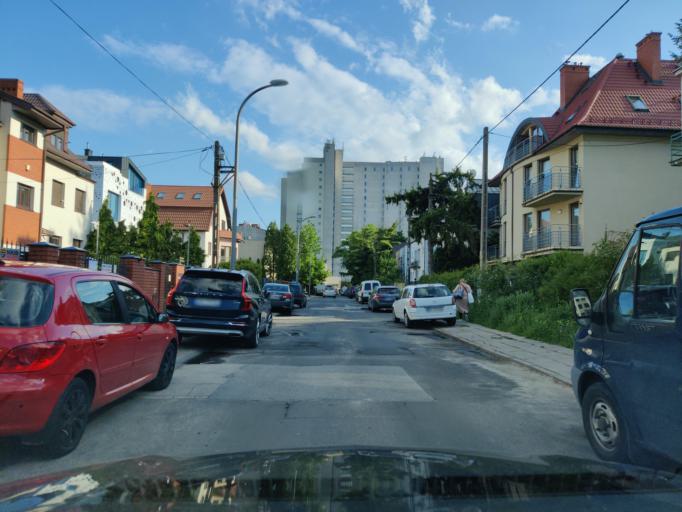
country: PL
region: Masovian Voivodeship
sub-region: Warszawa
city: Mokotow
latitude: 52.1757
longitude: 21.0225
